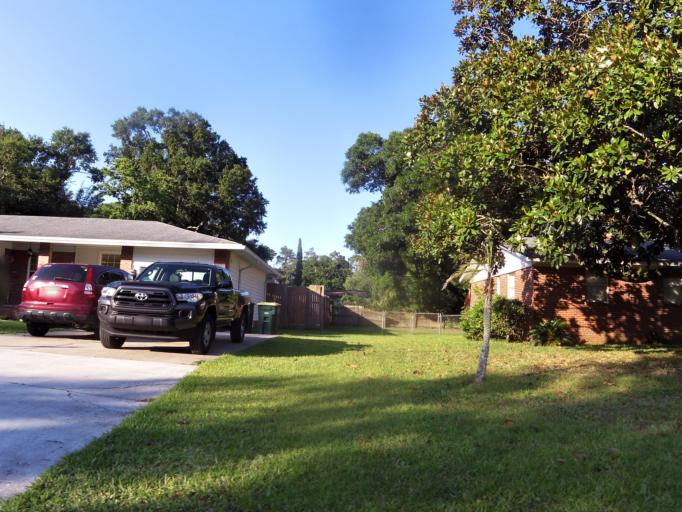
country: US
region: Florida
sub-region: Duval County
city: Jacksonville
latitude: 30.2371
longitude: -81.6176
